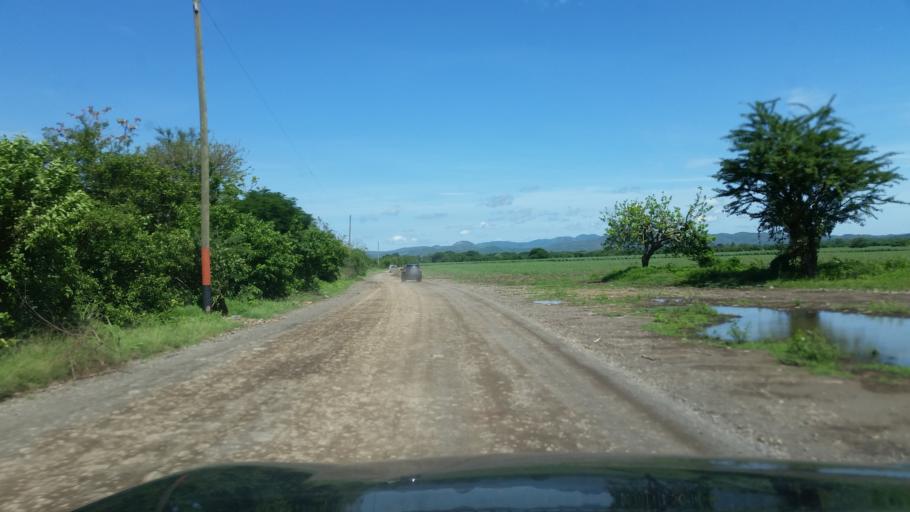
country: NI
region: Chinandega
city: Puerto Morazan
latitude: 12.7732
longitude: -87.1123
